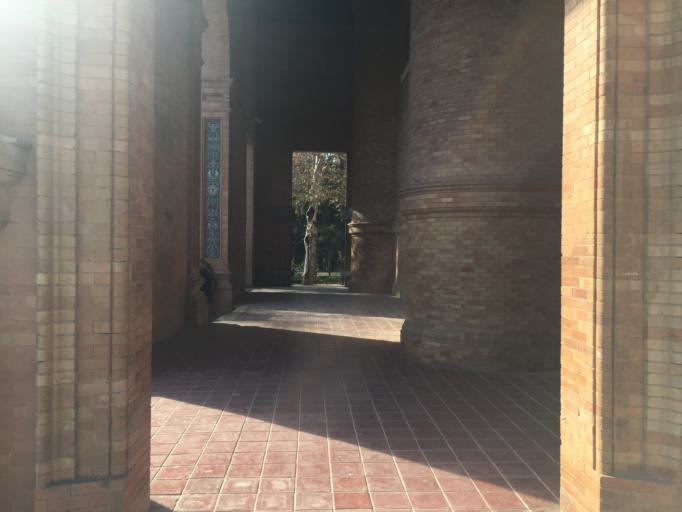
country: ES
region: Andalusia
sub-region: Provincia de Sevilla
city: Sevilla
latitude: 37.3779
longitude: -5.9878
